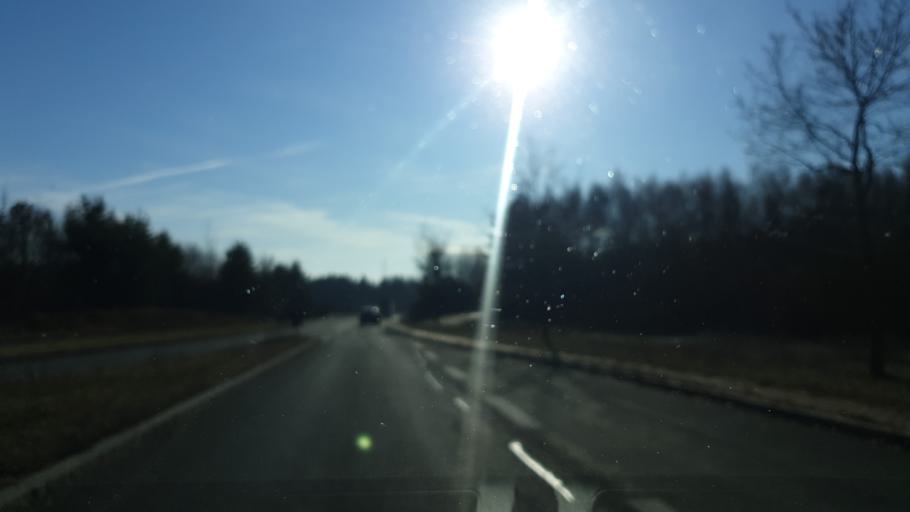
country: DE
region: Saxony
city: Bad Brambach
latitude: 50.1757
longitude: 12.3146
